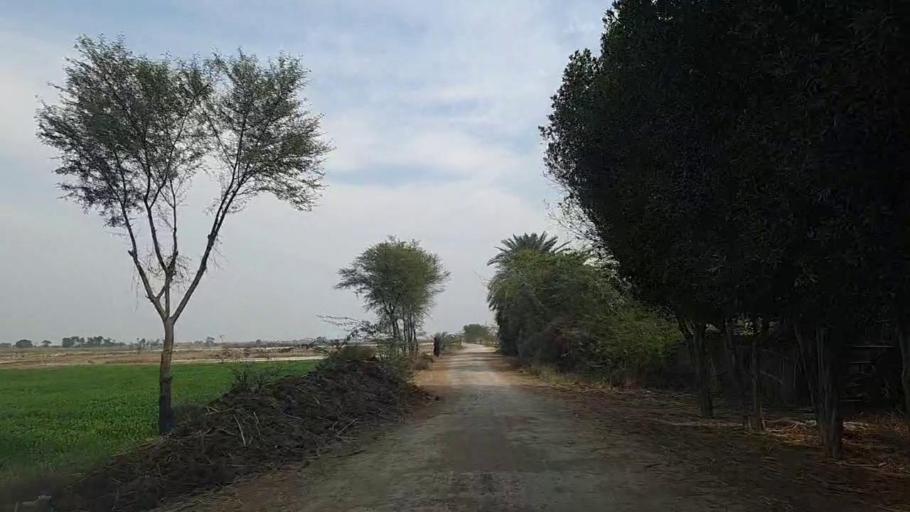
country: PK
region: Sindh
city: Daur
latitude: 26.4976
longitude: 68.3739
